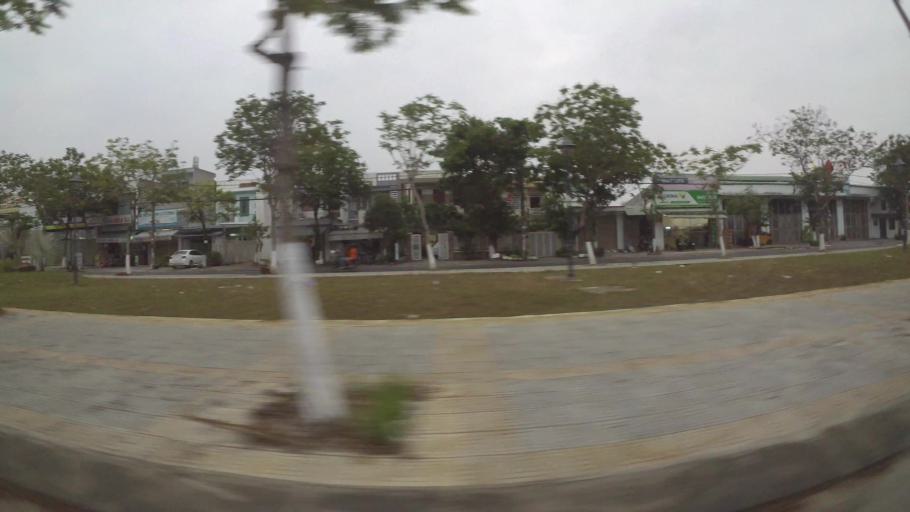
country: VN
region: Da Nang
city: Thanh Khe
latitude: 16.0531
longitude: 108.1776
